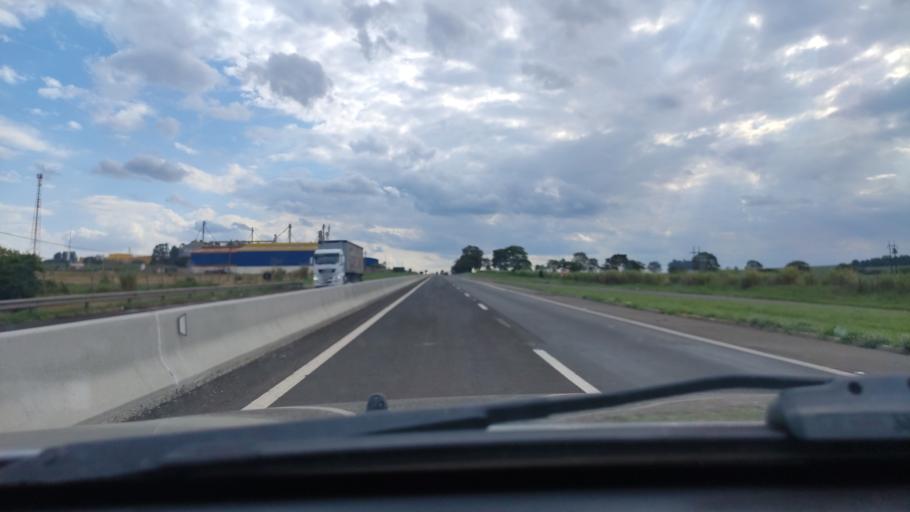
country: BR
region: Sao Paulo
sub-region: Santa Cruz Do Rio Pardo
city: Santa Cruz do Rio Pardo
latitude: -22.8719
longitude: -49.6583
